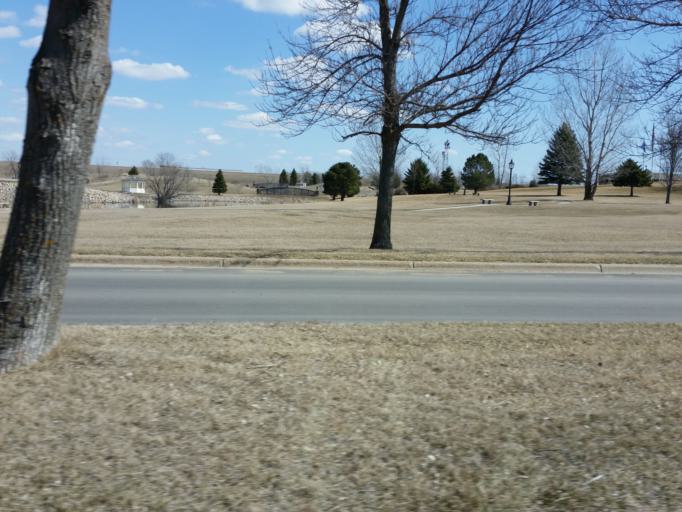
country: US
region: South Dakota
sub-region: Codington County
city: Watertown
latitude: 44.8879
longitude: -97.0630
